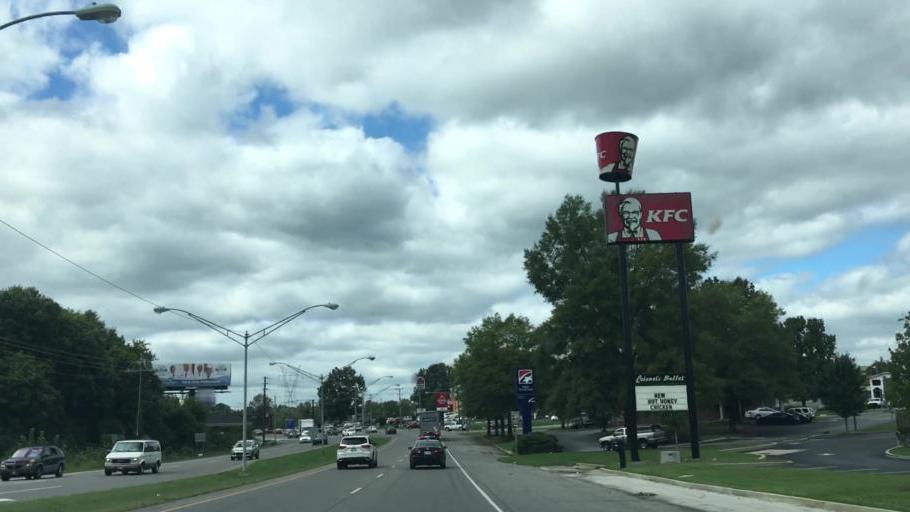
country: US
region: Tennessee
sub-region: Maury County
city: Columbia
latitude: 35.6029
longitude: -87.0649
